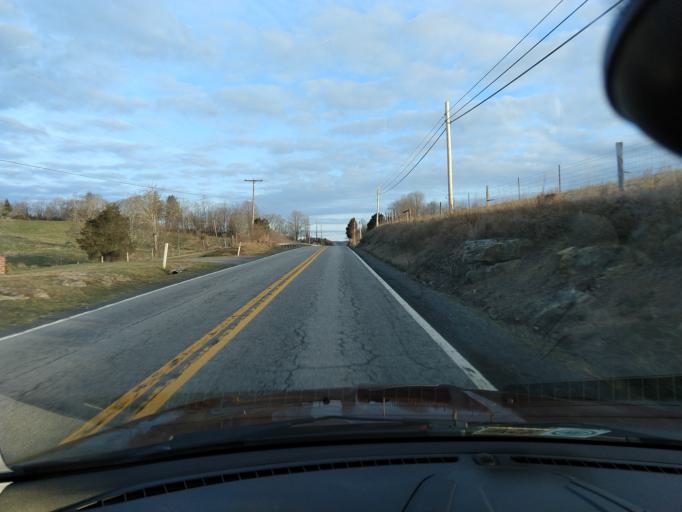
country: US
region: West Virginia
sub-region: Greenbrier County
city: Lewisburg
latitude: 37.9509
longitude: -80.3759
